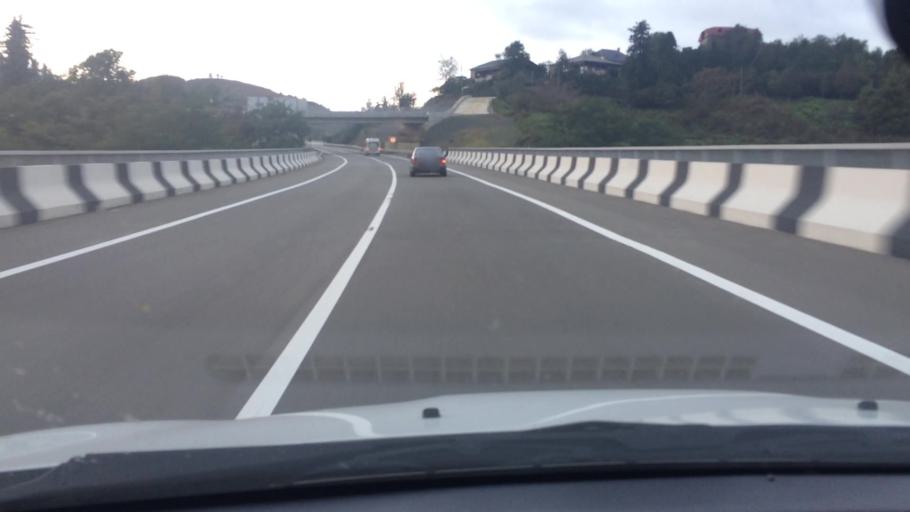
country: GE
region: Ajaria
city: Makhinjauri
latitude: 41.7171
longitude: 41.7518
